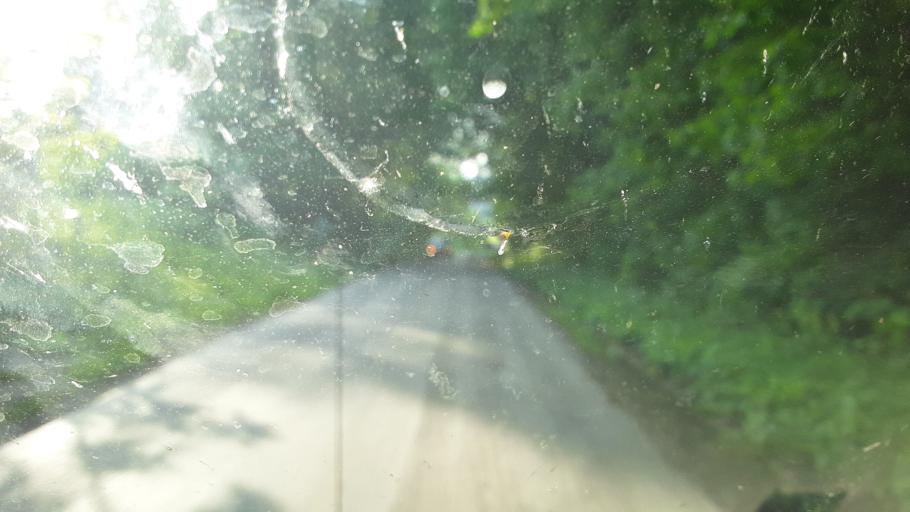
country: US
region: Ohio
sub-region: Wayne County
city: Shreve
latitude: 40.6659
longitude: -82.0841
